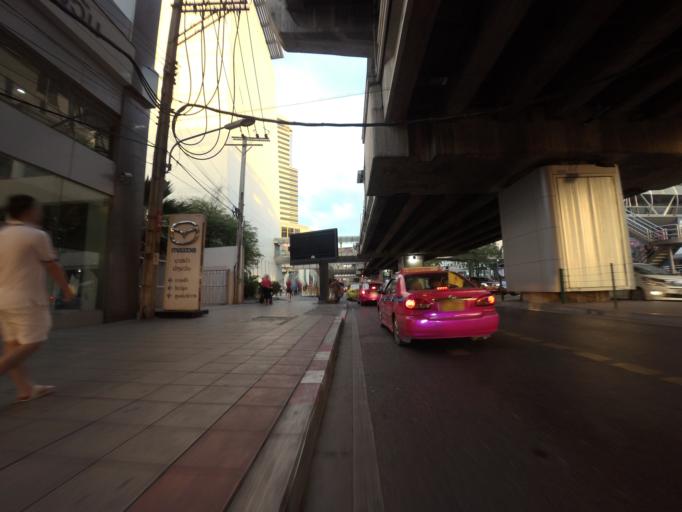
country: TH
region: Bangkok
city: Pathum Wan
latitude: 13.7465
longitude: 100.5296
